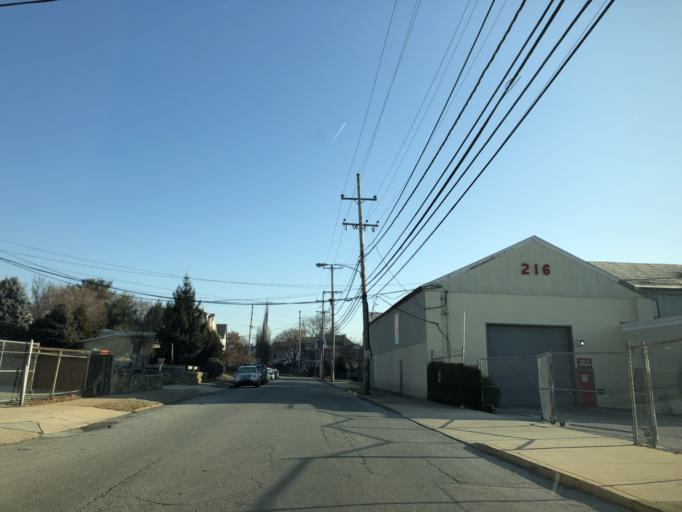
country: US
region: Pennsylvania
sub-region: Chester County
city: Downingtown
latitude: 40.0064
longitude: -75.7006
